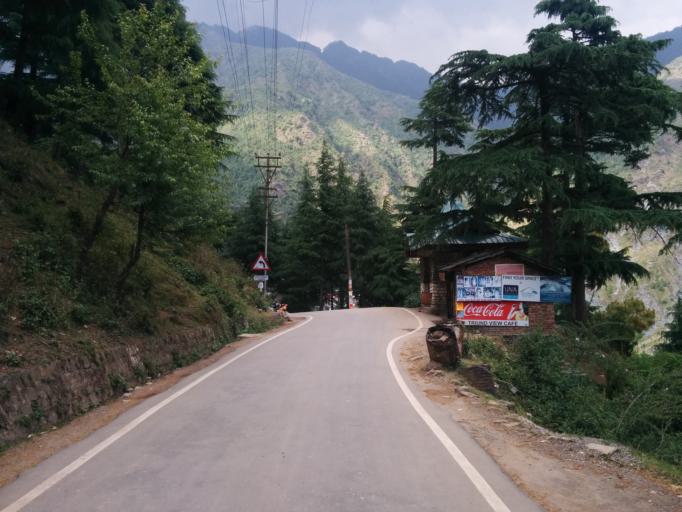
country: IN
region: Himachal Pradesh
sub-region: Kangra
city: Dharmsala
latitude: 32.2404
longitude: 76.3322
